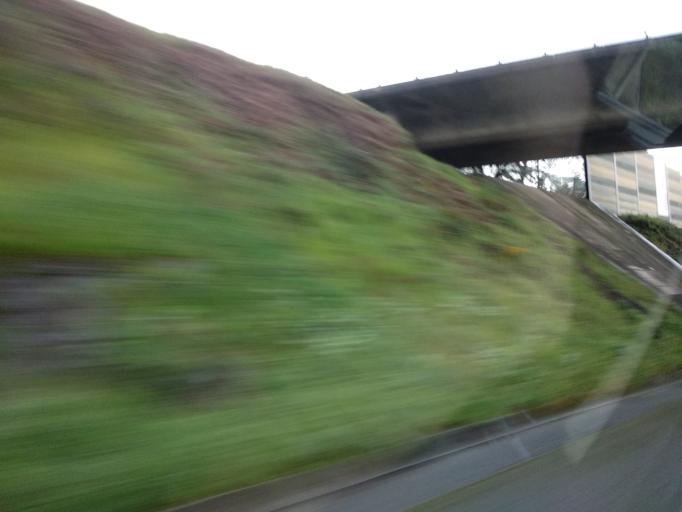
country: PT
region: Braga
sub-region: Braga
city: Oliveira
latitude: 41.4933
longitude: -8.4650
